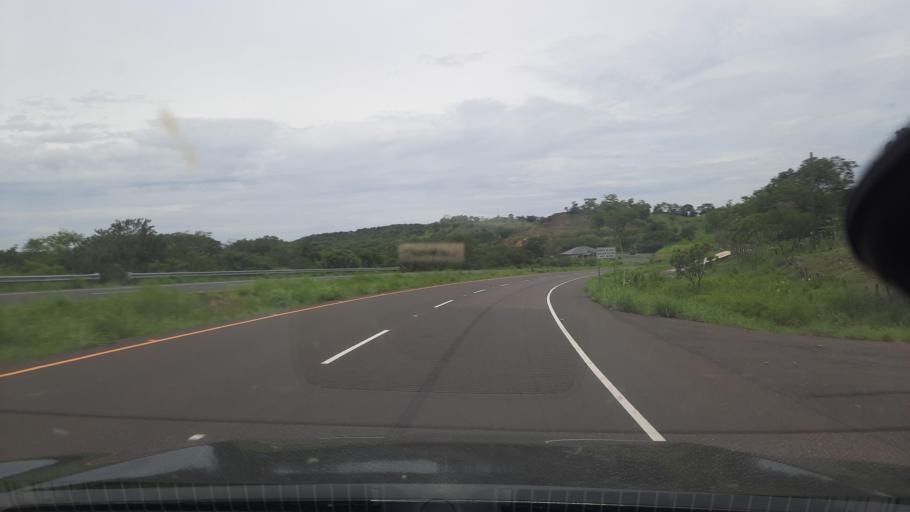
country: HN
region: Valle
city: Aramecina
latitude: 13.7590
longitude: -87.7098
